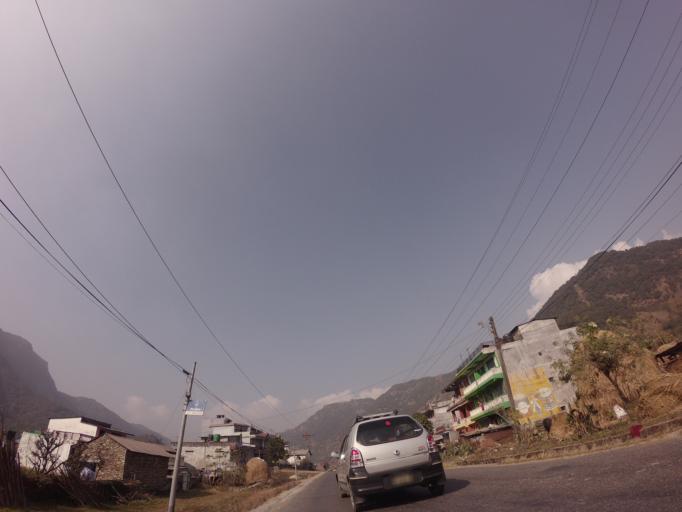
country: NP
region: Western Region
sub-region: Gandaki Zone
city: Pokhara
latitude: 28.2807
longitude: 83.9285
